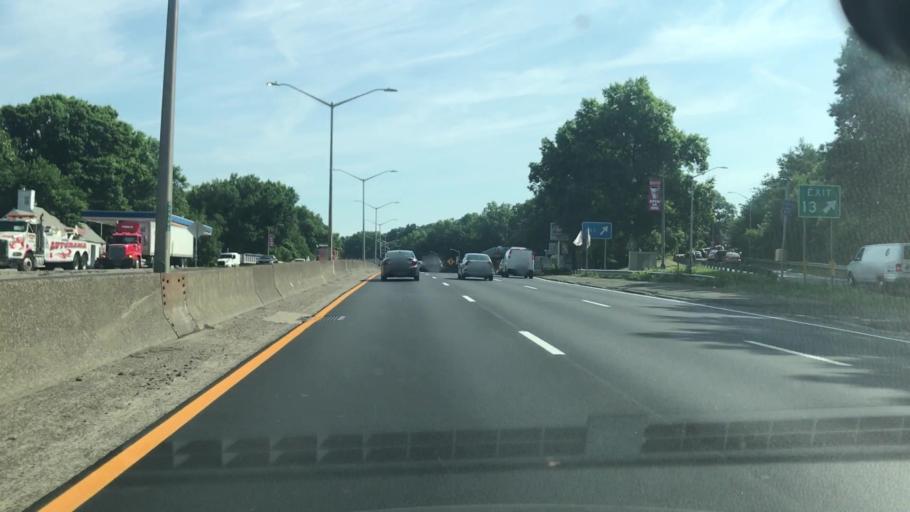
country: US
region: New York
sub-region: Westchester County
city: Yonkers
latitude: 40.8942
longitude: -73.8828
